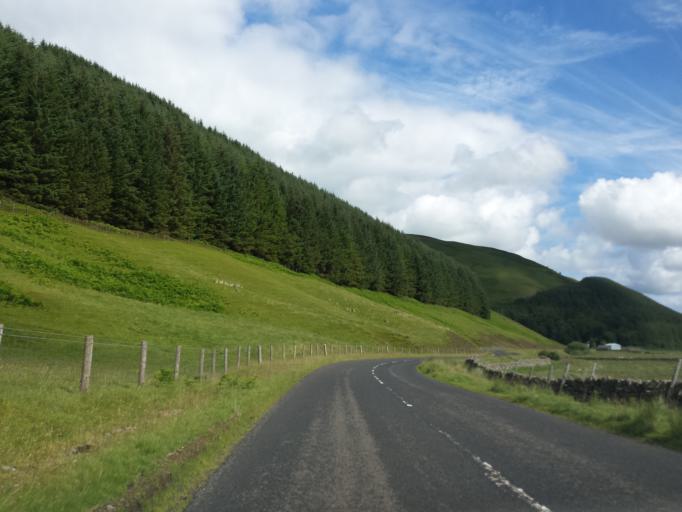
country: GB
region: Scotland
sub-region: The Scottish Borders
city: Peebles
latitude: 55.4524
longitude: -3.2215
